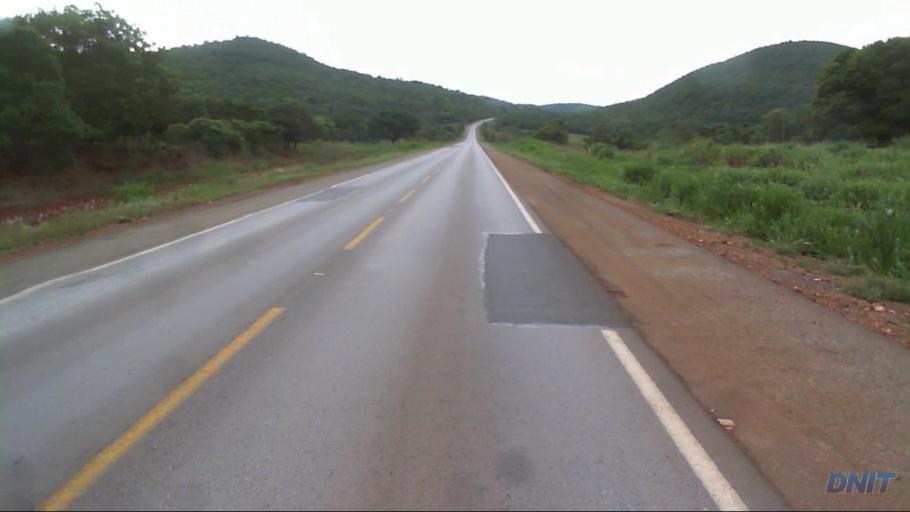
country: BR
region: Goias
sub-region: Barro Alto
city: Barro Alto
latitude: -14.9098
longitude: -48.9578
